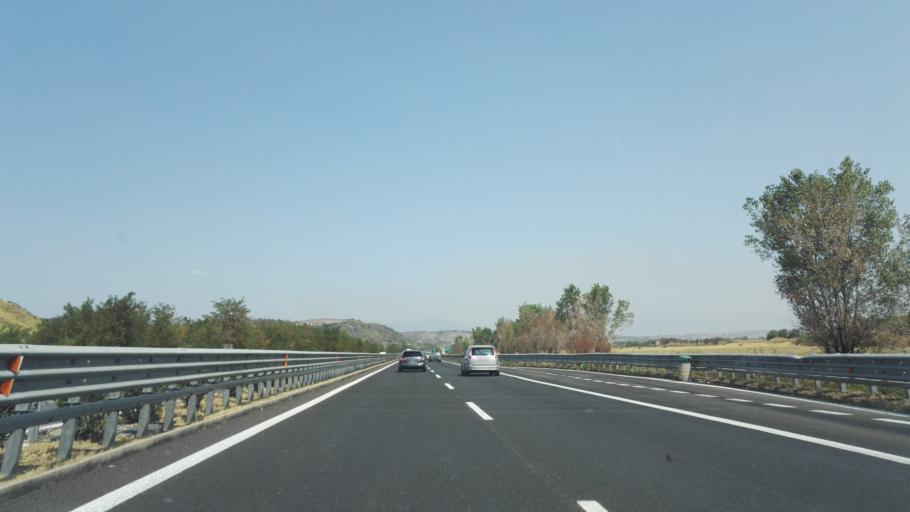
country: IT
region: Calabria
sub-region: Provincia di Cosenza
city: Taverna
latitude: 39.4674
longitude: 16.2199
